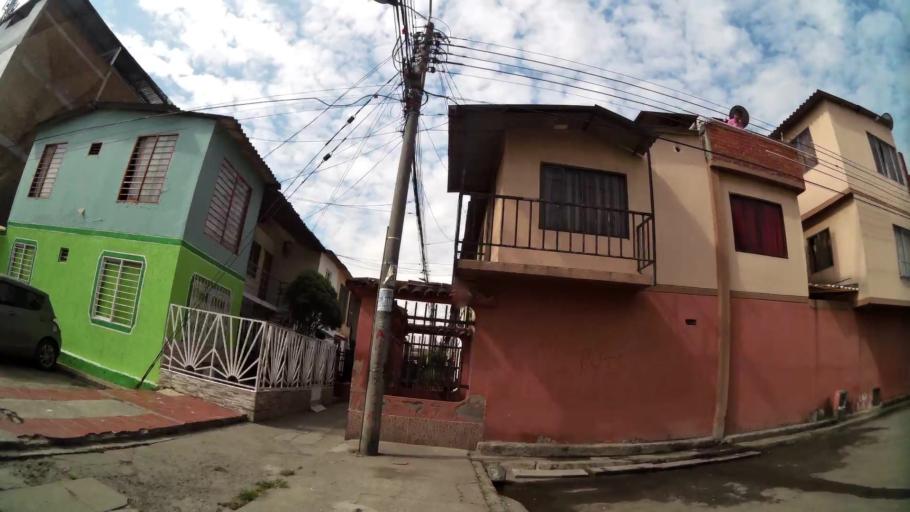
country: CO
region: Valle del Cauca
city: Cali
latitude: 3.4932
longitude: -76.4967
